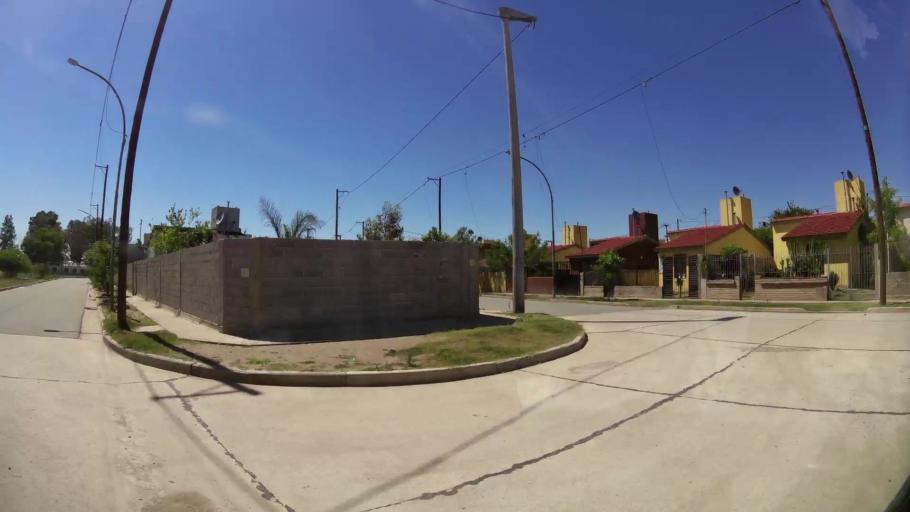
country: AR
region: Cordoba
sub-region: Departamento de Capital
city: Cordoba
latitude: -31.4079
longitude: -64.1362
